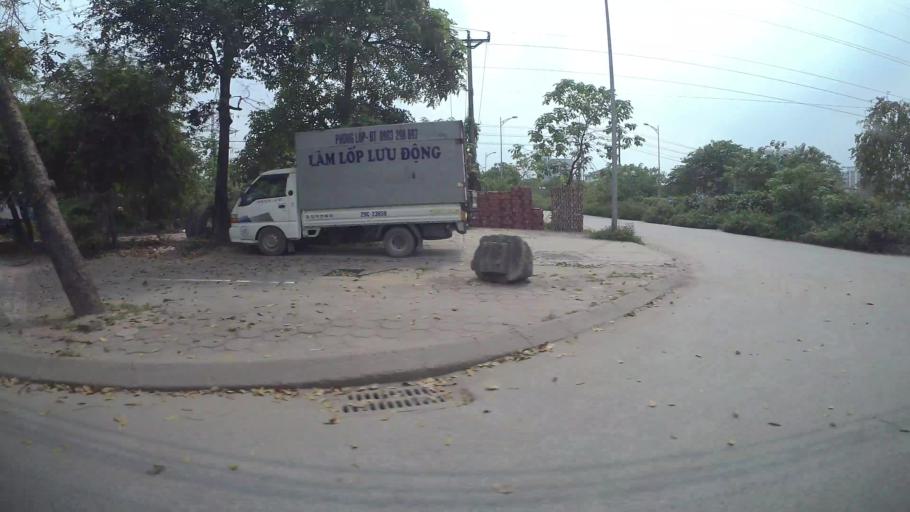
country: VN
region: Ha Noi
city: Trau Quy
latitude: 21.0689
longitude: 105.9030
